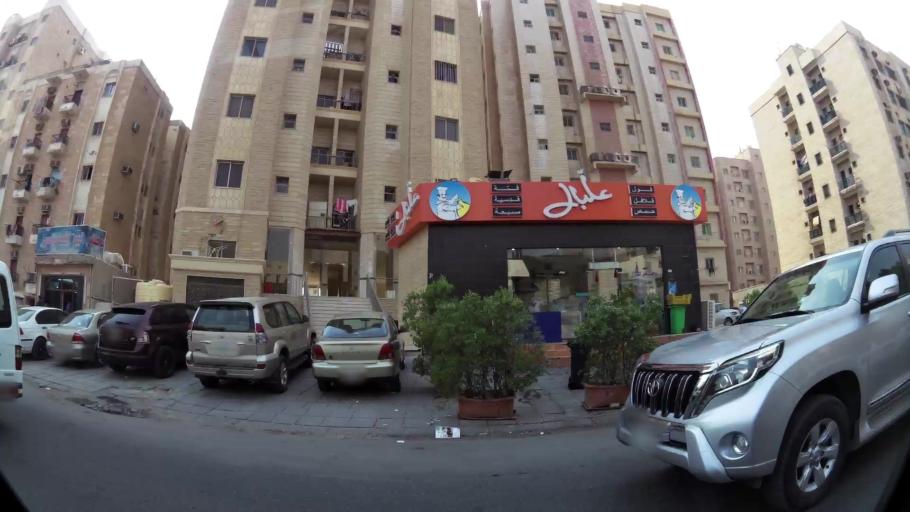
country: KW
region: Al Farwaniyah
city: Al Farwaniyah
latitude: 29.2764
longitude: 47.9551
